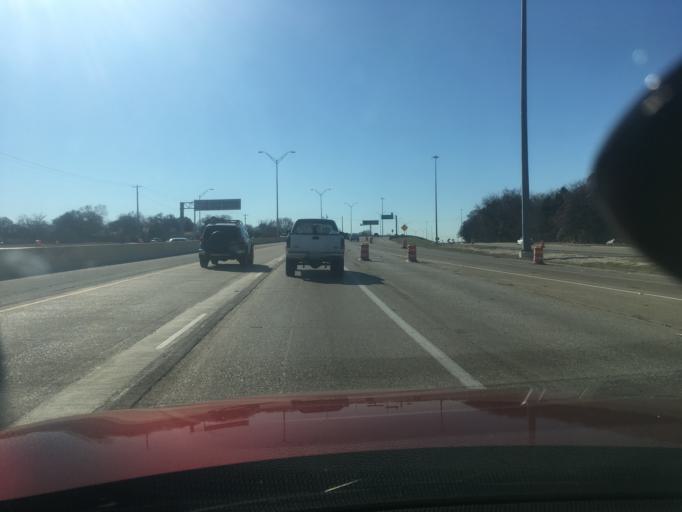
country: US
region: Texas
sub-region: Dallas County
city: Cockrell Hill
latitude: 32.6876
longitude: -96.8479
